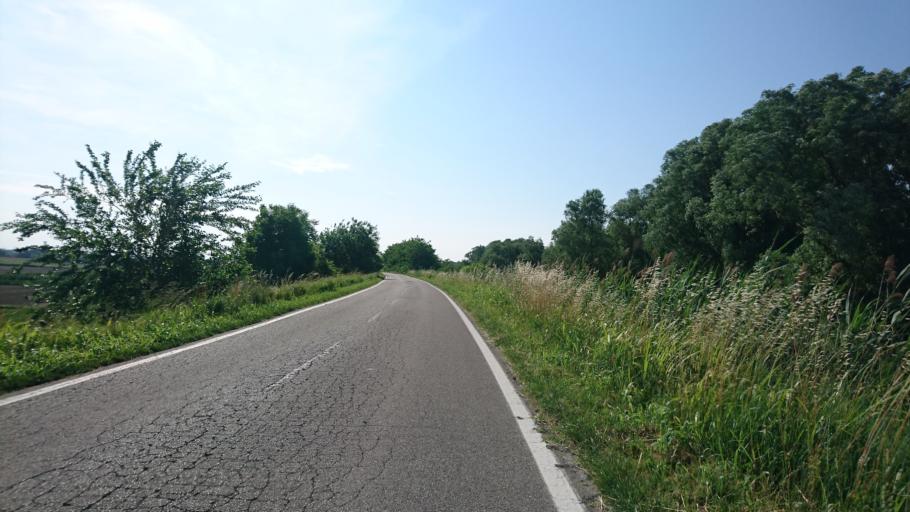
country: IT
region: Veneto
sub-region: Provincia di Verona
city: Villa Bartolomea
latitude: 45.1669
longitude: 11.3541
